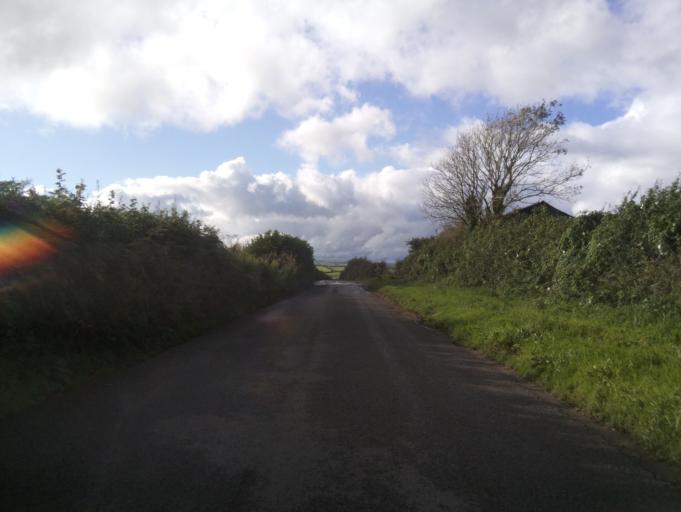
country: GB
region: England
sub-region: Devon
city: South Brent
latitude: 50.3965
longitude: -3.7792
